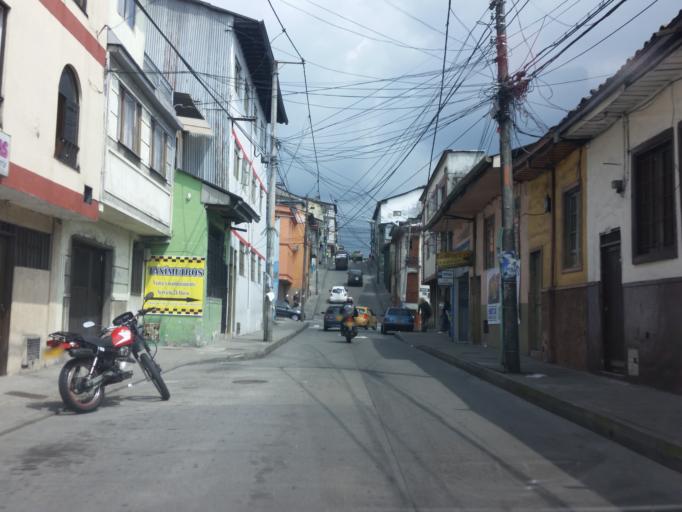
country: CO
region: Caldas
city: Manizales
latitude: 5.0660
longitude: -75.5135
